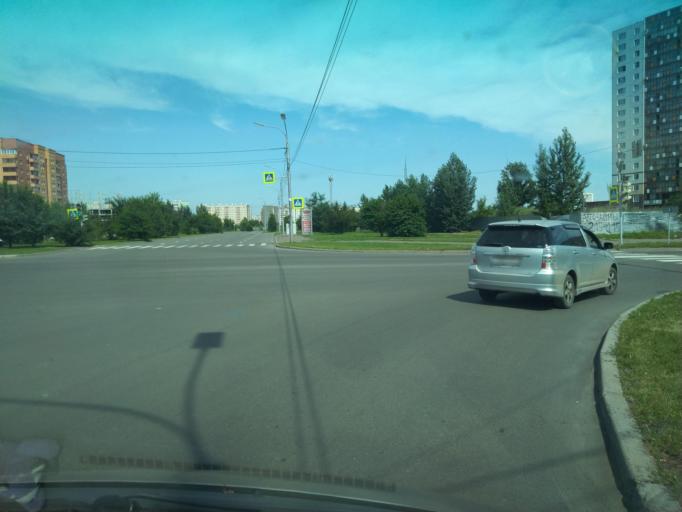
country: RU
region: Krasnoyarskiy
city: Solnechnyy
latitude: 56.0546
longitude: 92.9196
